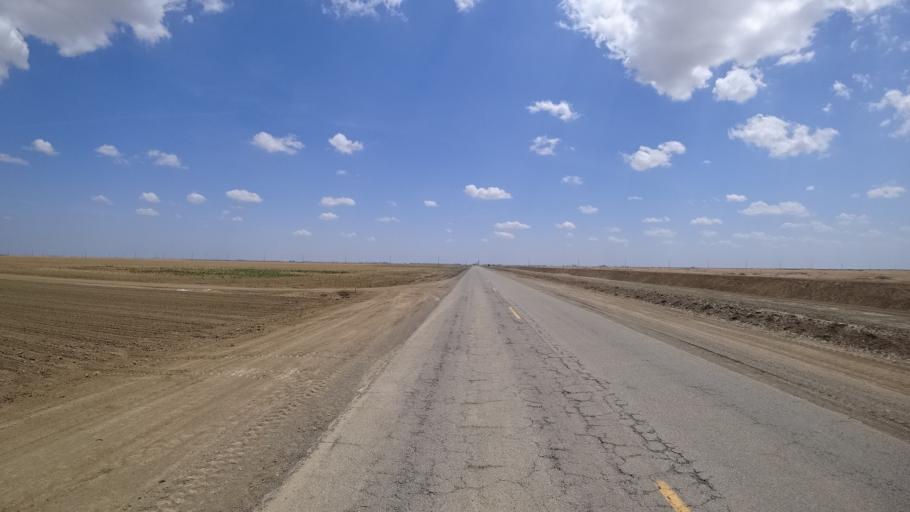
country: US
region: California
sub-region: Kings County
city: Lemoore Station
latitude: 36.1894
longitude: -119.9144
